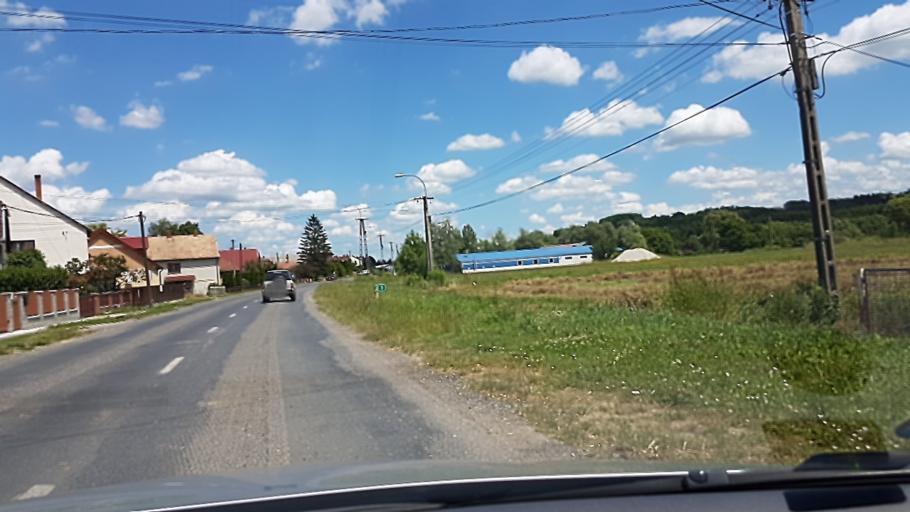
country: HU
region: Zala
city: Zalaegerszeg
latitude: 46.8456
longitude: 16.7706
